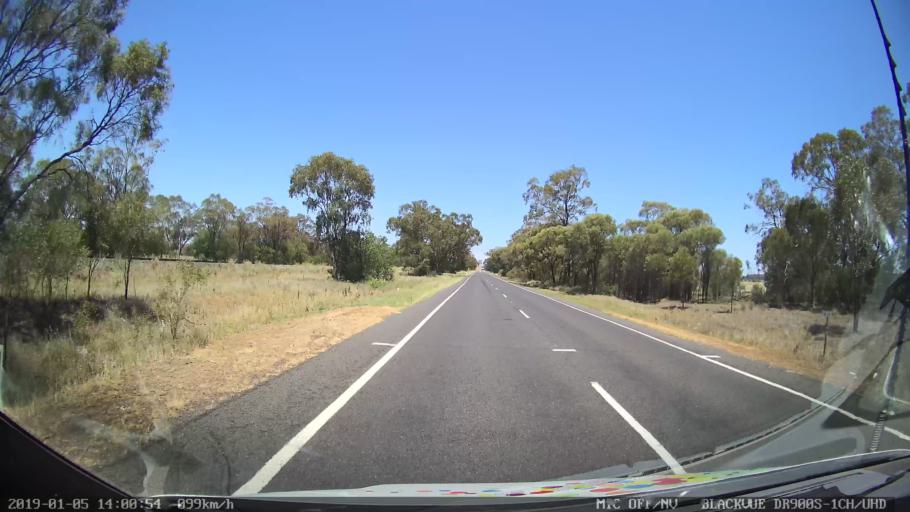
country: AU
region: New South Wales
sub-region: Gunnedah
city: Gunnedah
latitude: -31.1643
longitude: 150.3183
